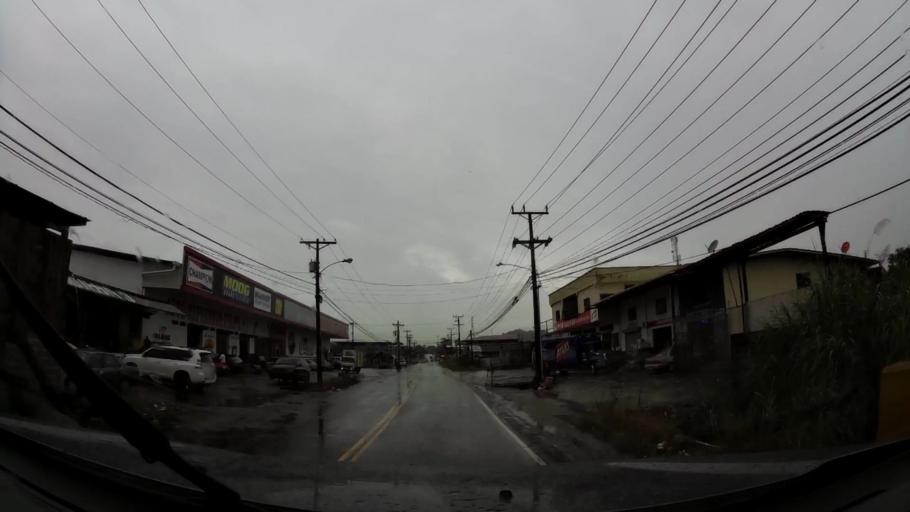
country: PA
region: Colon
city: Puerto Pilon
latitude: 9.3547
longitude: -79.8025
